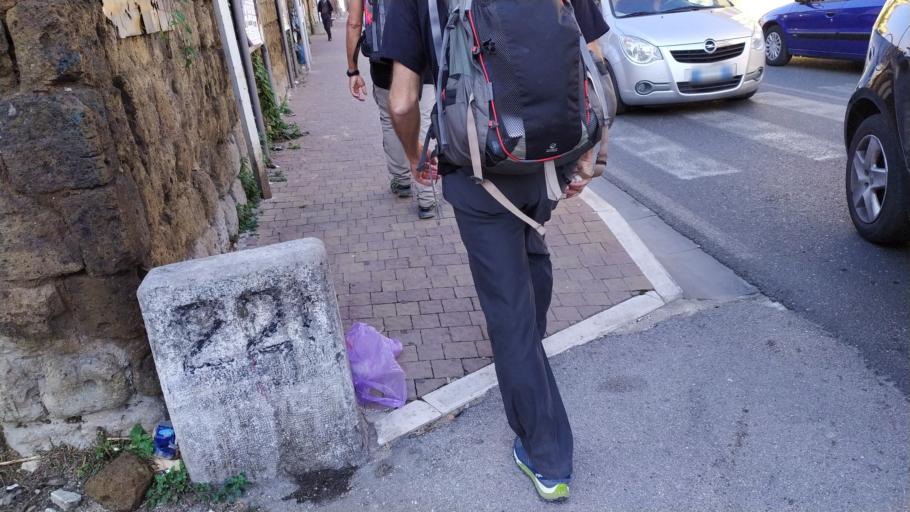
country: IT
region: Campania
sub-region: Provincia di Caserta
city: Maddaloni
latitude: 41.0347
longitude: 14.3875
